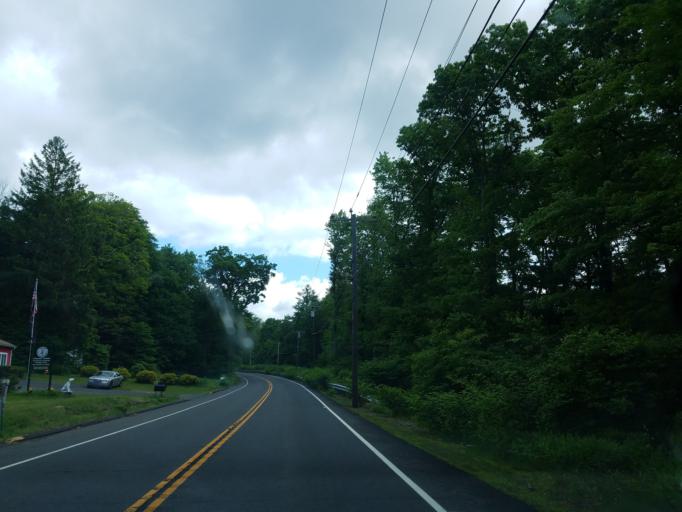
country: US
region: Connecticut
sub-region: New Haven County
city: Prospect
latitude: 41.4612
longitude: -72.9663
